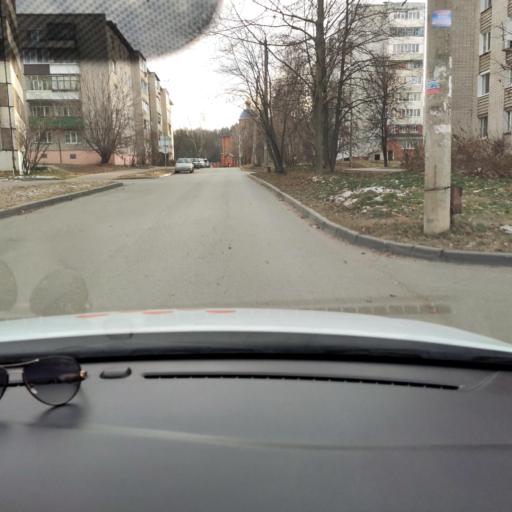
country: RU
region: Tatarstan
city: Vysokaya Gora
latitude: 55.8594
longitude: 49.2230
